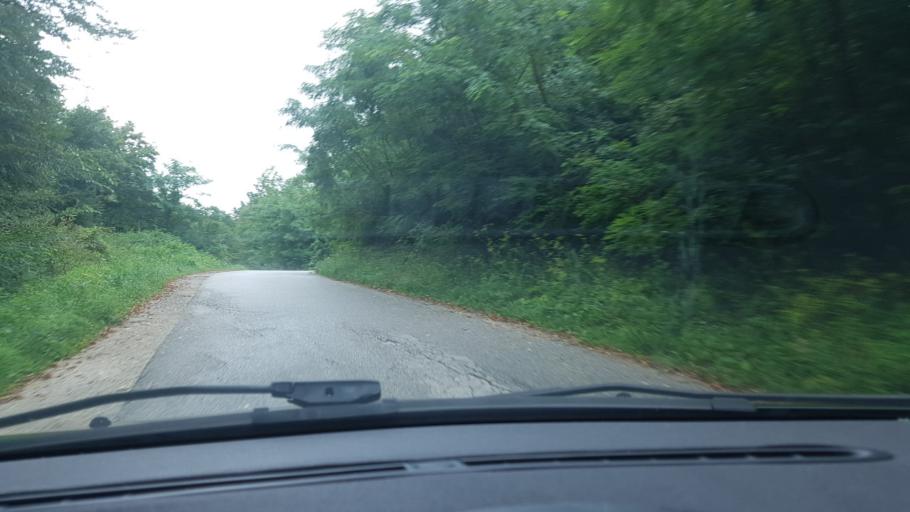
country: HR
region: Karlovacka
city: Ozalj
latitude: 45.6045
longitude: 15.5379
